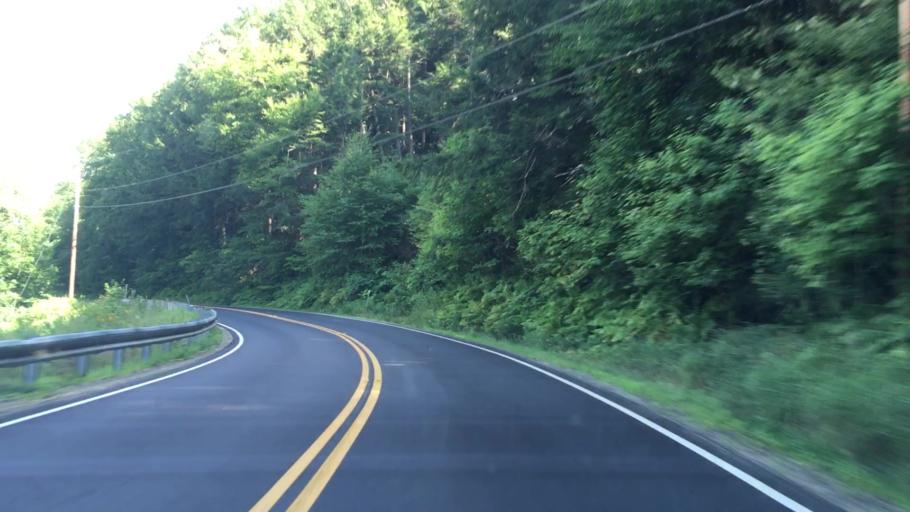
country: US
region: New Hampshire
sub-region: Grafton County
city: North Haverhill
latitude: 44.1204
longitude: -71.9216
